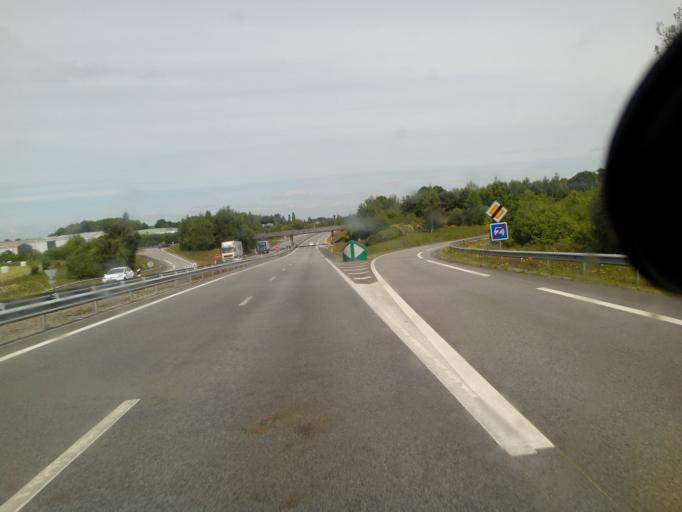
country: FR
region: Brittany
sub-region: Departement d'Ille-et-Vilaine
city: Grand-Fougeray
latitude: 47.7434
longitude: -1.7144
